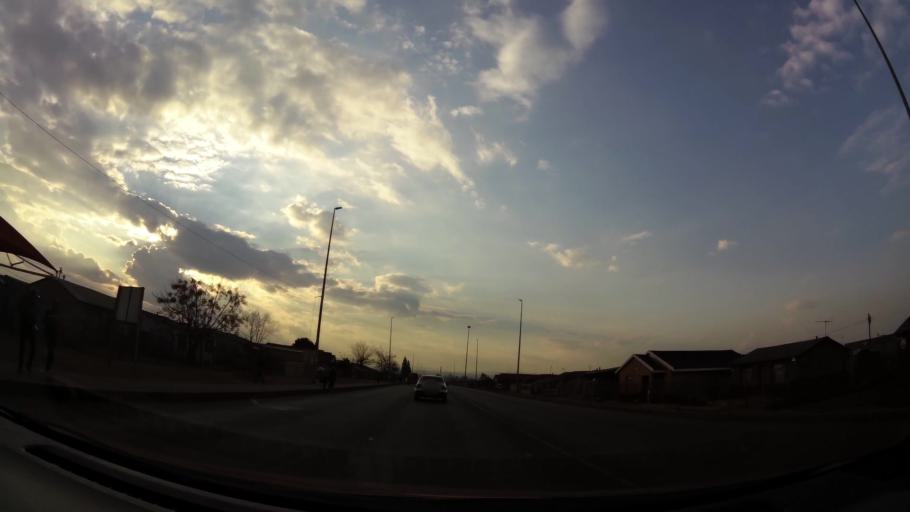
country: ZA
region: Gauteng
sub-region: City of Johannesburg Metropolitan Municipality
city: Orange Farm
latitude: -26.5798
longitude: 27.8421
